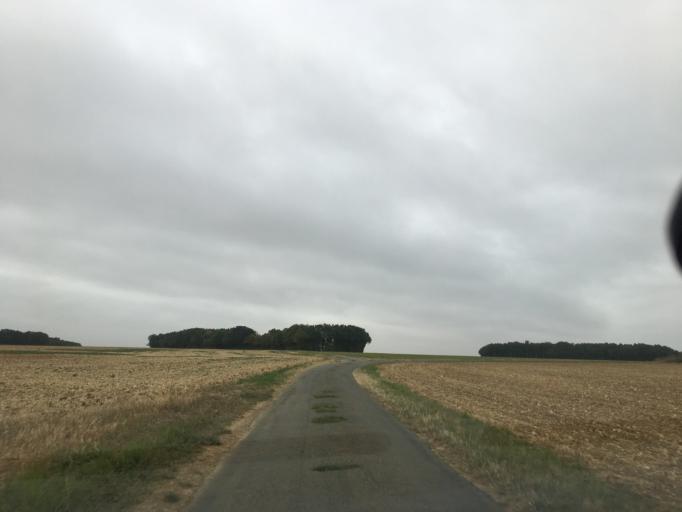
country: FR
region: Poitou-Charentes
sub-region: Departement des Deux-Sevres
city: Beauvoir-sur-Niort
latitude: 46.0873
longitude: -0.5241
